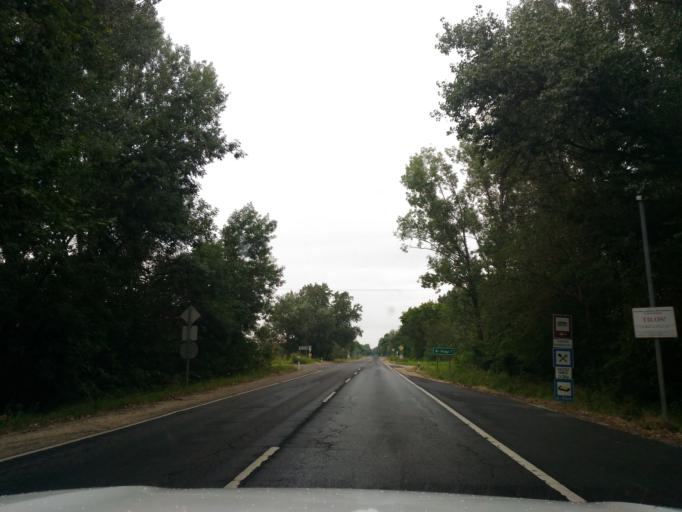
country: HU
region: Pest
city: Ocsa
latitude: 47.2814
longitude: 19.1979
